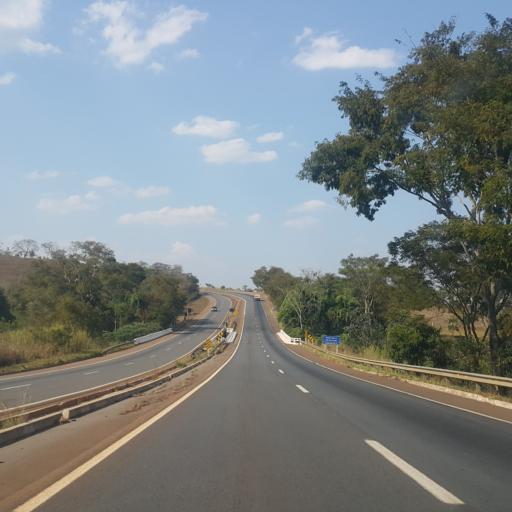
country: BR
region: Goias
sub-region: Abadiania
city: Abadiania
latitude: -16.2977
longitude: -48.8059
